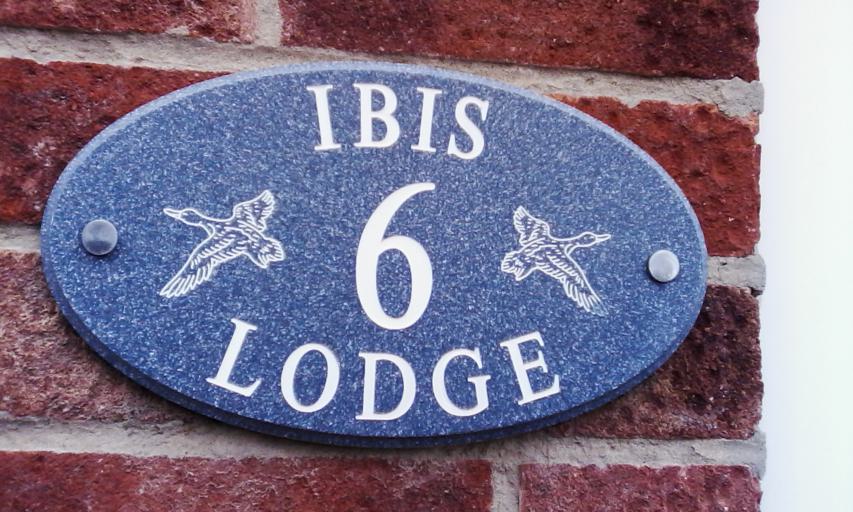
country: GB
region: England
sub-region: Nottinghamshire
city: Arnold
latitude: 52.9756
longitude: -1.0929
